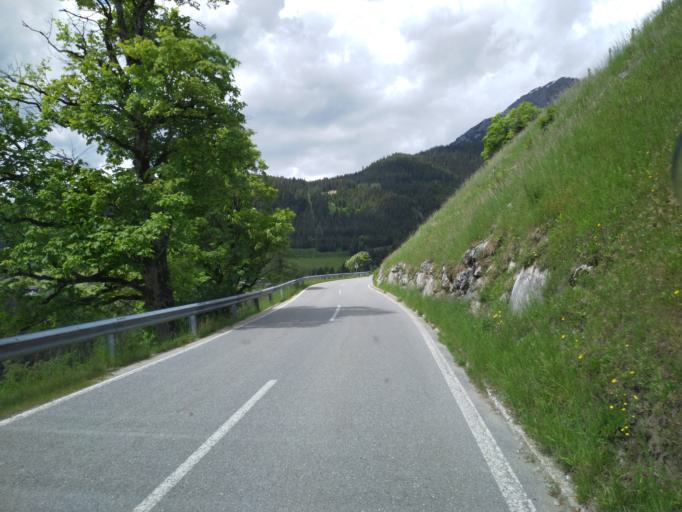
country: AT
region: Salzburg
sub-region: Politischer Bezirk Sankt Johann im Pongau
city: Filzmoos
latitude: 47.4316
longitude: 13.5813
